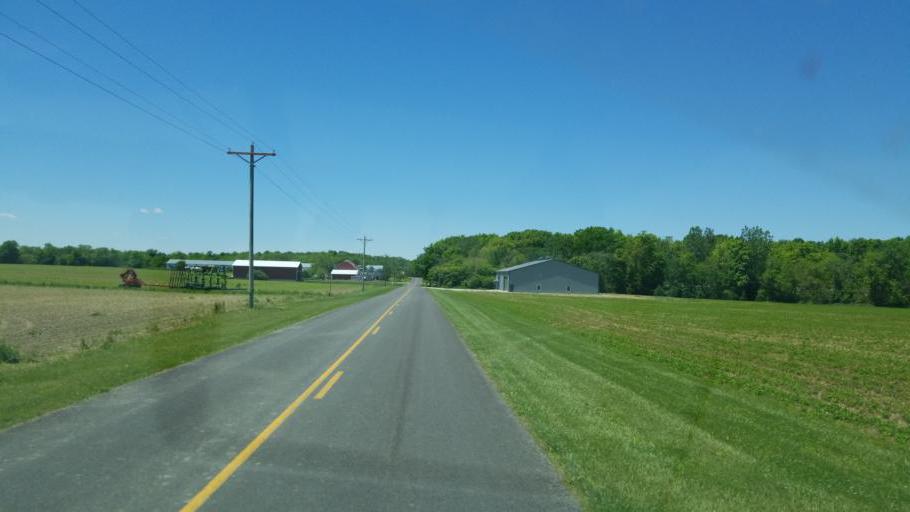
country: US
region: Ohio
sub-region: Mercer County
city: Fort Recovery
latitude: 40.3673
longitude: -84.7899
